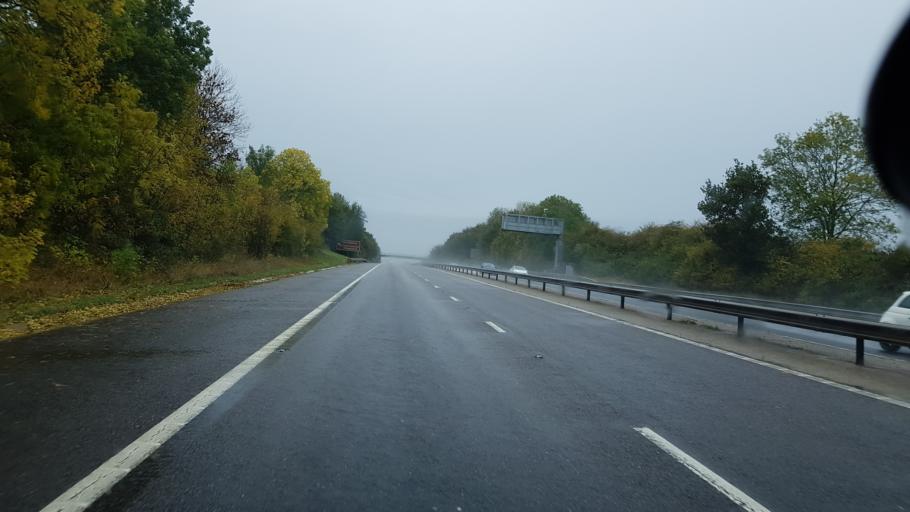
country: GB
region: England
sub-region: Worcestershire
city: Bredon
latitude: 52.0417
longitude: -2.1495
